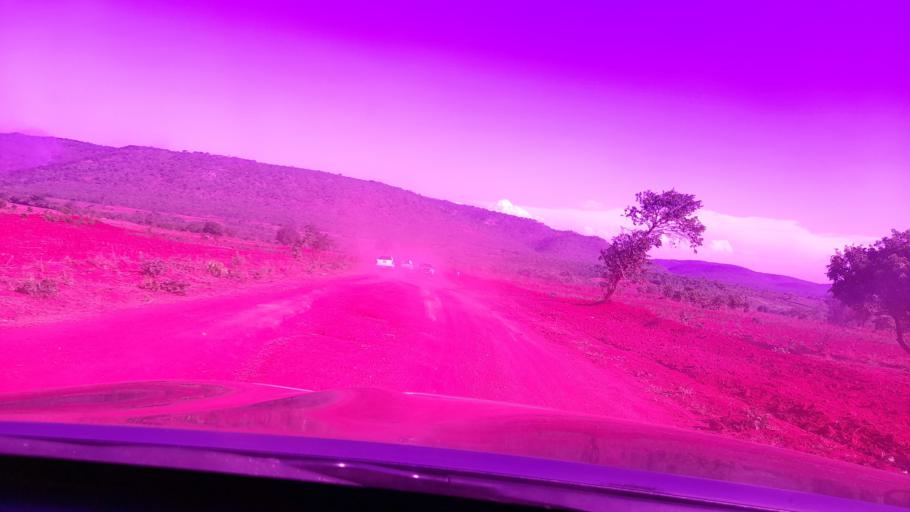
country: ZM
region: Northern
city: Mpika
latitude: -11.7294
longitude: 31.4798
